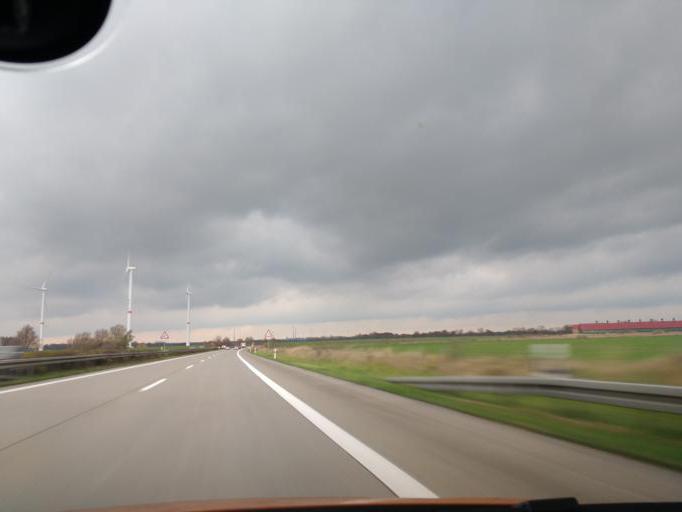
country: DE
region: Brandenburg
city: Heiligengrabe
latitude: 53.1804
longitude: 12.3004
